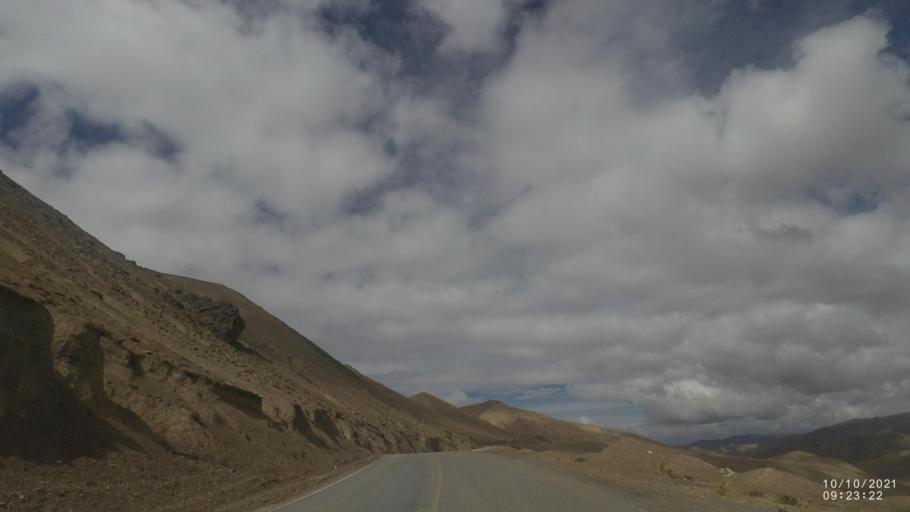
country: BO
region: La Paz
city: Quime
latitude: -17.0842
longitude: -67.3021
